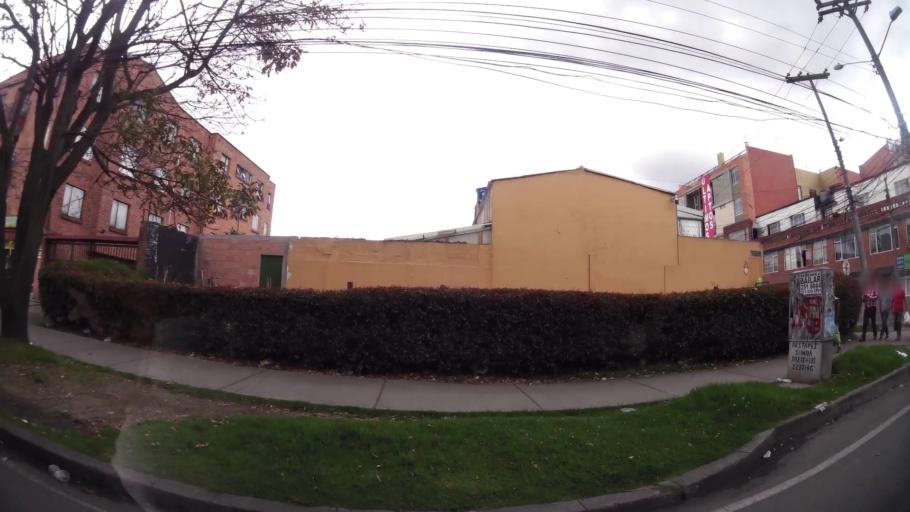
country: CO
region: Bogota D.C.
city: Barrio San Luis
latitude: 4.7036
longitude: -74.0923
